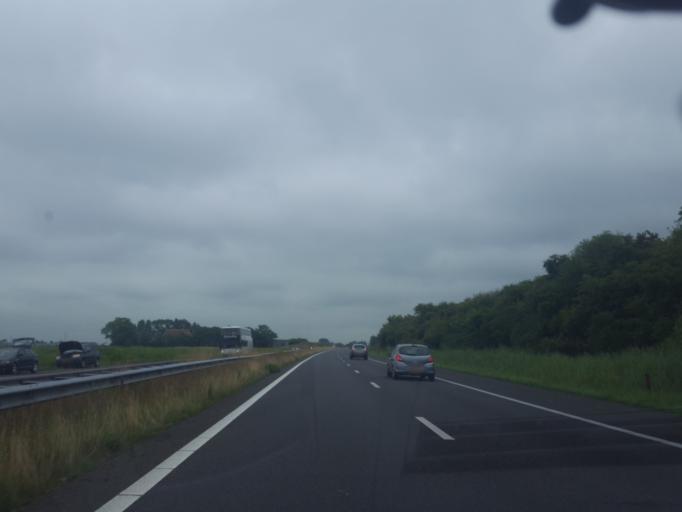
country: NL
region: Friesland
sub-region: Gemeente Boarnsterhim
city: Reduzum
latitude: 53.1112
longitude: 5.8135
